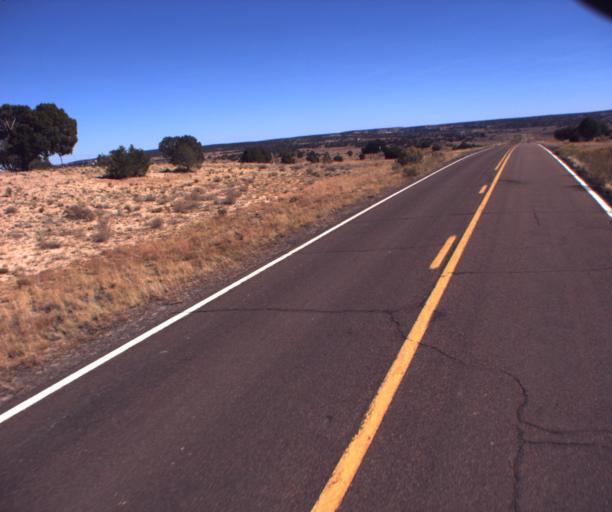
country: US
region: Arizona
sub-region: Apache County
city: Ganado
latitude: 35.7532
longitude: -109.8906
